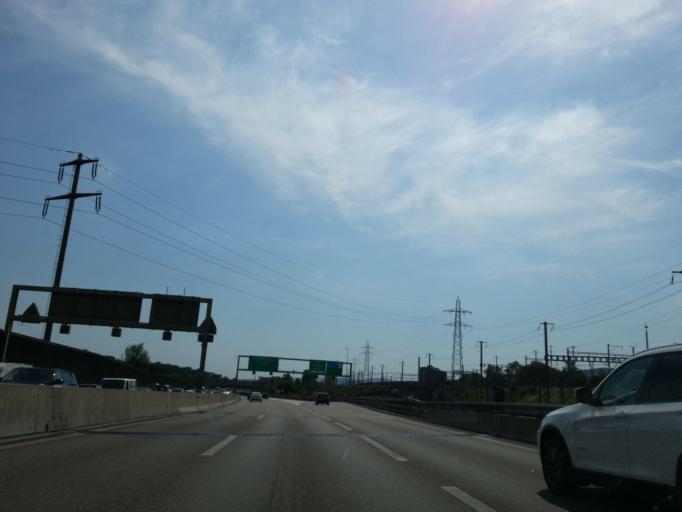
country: CH
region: Basel-Landschaft
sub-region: Bezirk Arlesheim
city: Birsfelden
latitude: 47.5423
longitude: 7.6228
